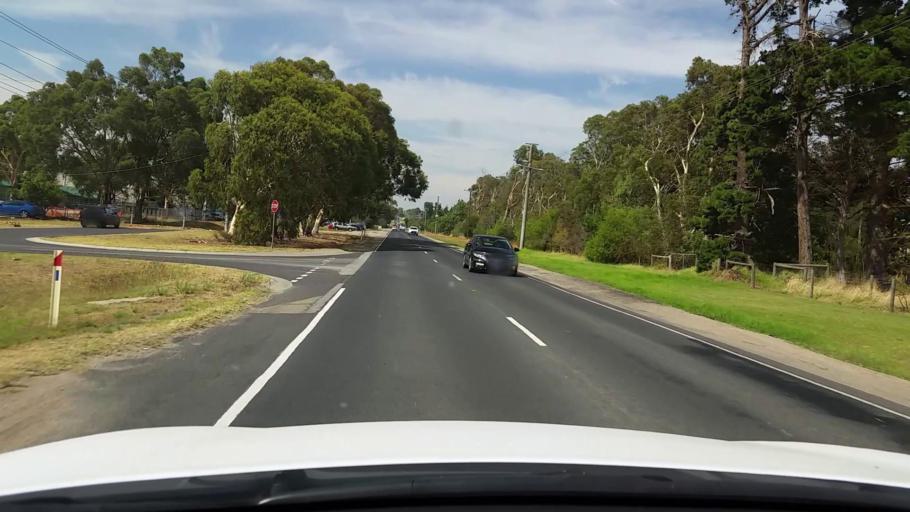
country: AU
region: Victoria
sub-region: Mornington Peninsula
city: Hastings
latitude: -38.2921
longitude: 145.1836
